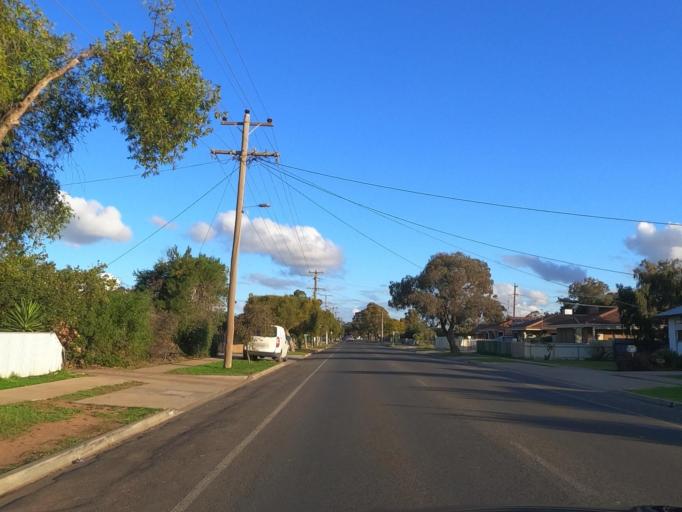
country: AU
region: Victoria
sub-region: Swan Hill
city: Swan Hill
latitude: -35.3423
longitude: 143.5439
